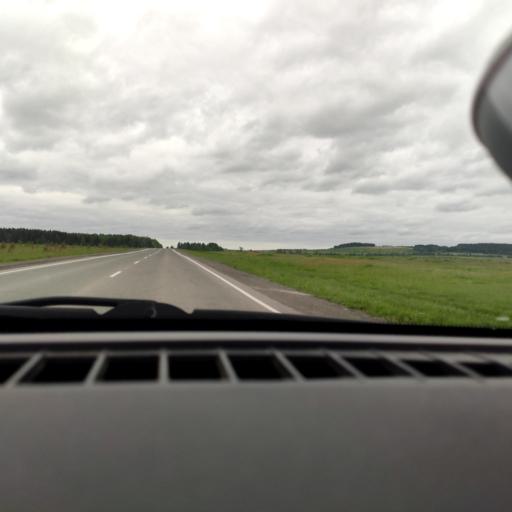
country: RU
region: Perm
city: Ust'-Kachka
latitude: 57.9697
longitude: 55.7250
